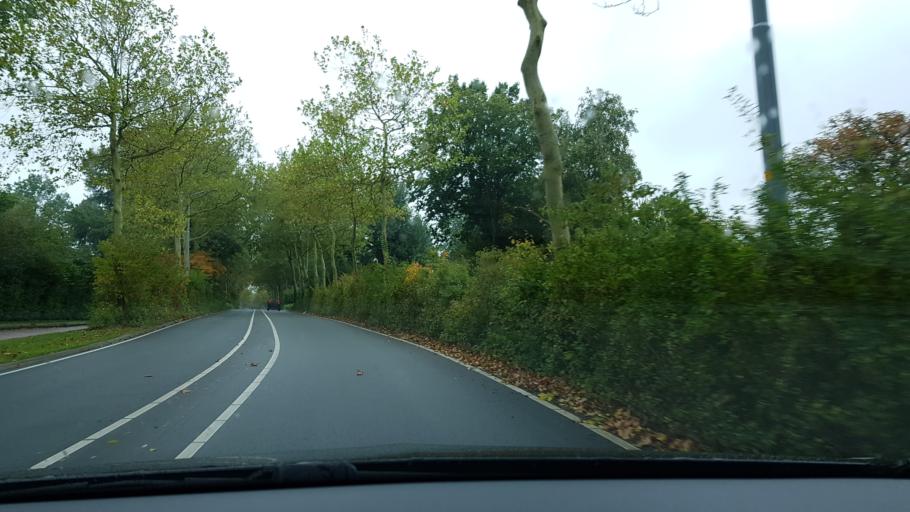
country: NL
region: North Holland
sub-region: Gemeente Haarlemmermeer
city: Hoofddorp
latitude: 52.3079
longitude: 4.6799
